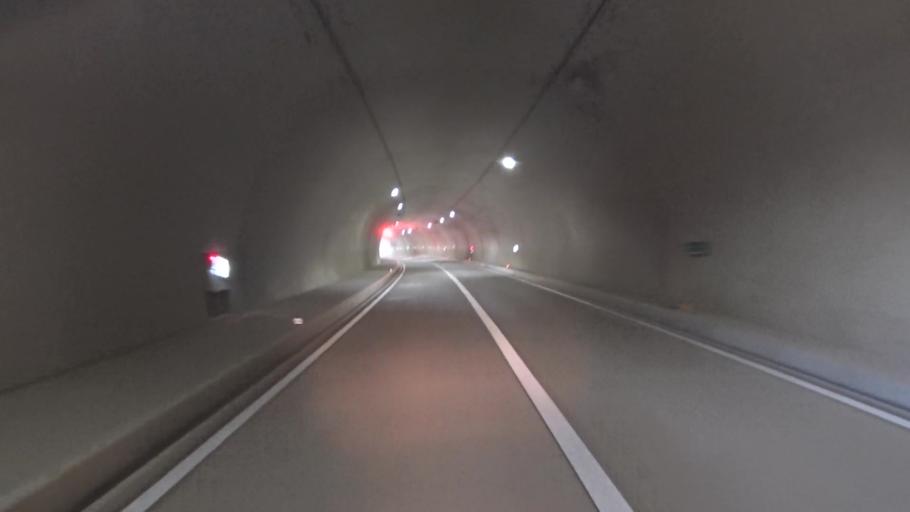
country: JP
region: Kyoto
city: Miyazu
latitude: 35.7398
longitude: 135.2549
